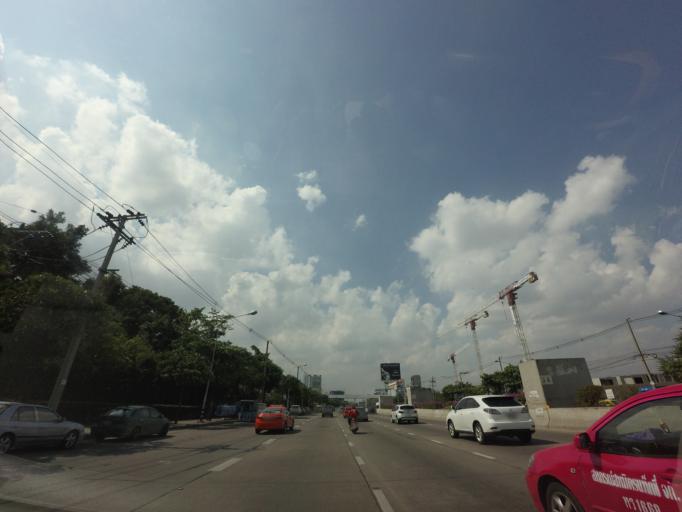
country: TH
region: Bangkok
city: Chatuchak
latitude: 13.8411
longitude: 100.5885
